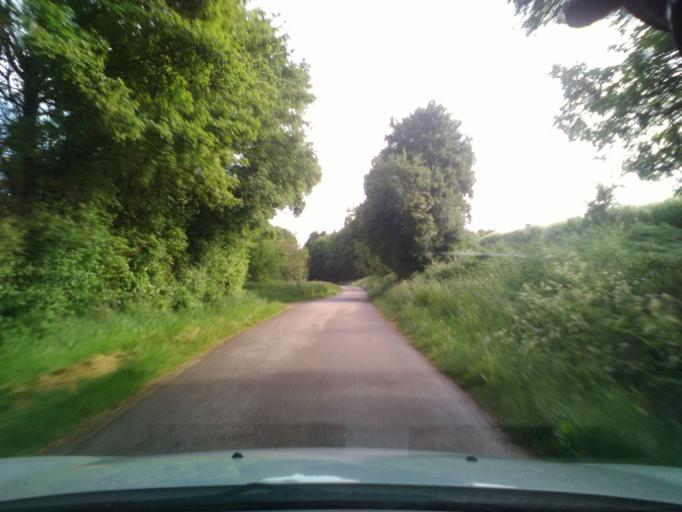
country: FR
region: Lorraine
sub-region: Departement des Vosges
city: Mirecourt
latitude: 48.3419
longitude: 6.1616
